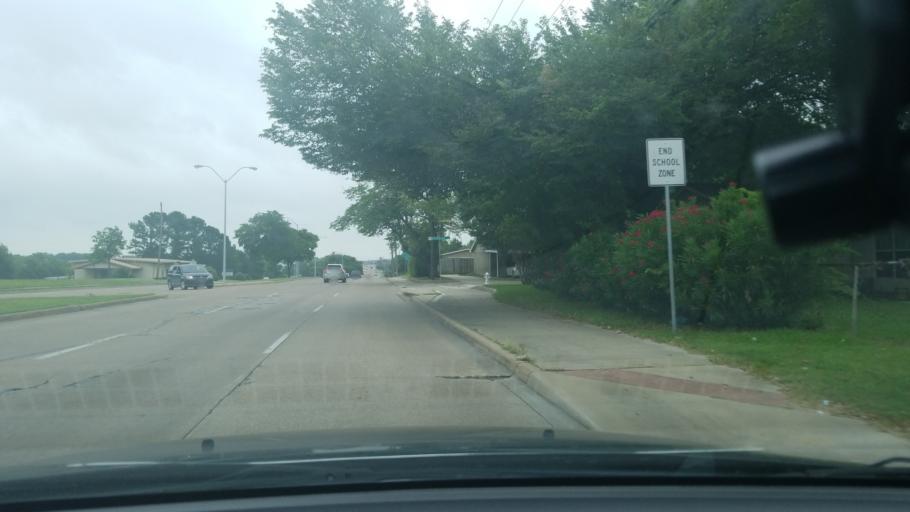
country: US
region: Texas
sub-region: Dallas County
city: Mesquite
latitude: 32.7875
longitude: -96.6316
